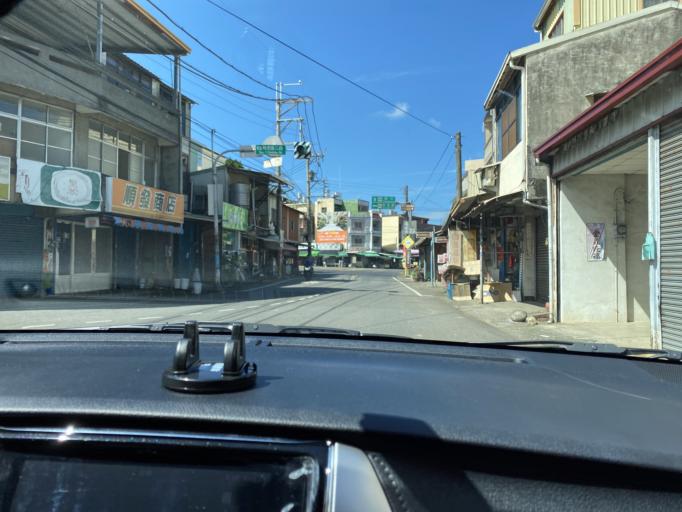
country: TW
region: Taiwan
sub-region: Nantou
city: Nantou
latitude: 23.8579
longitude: 120.6296
